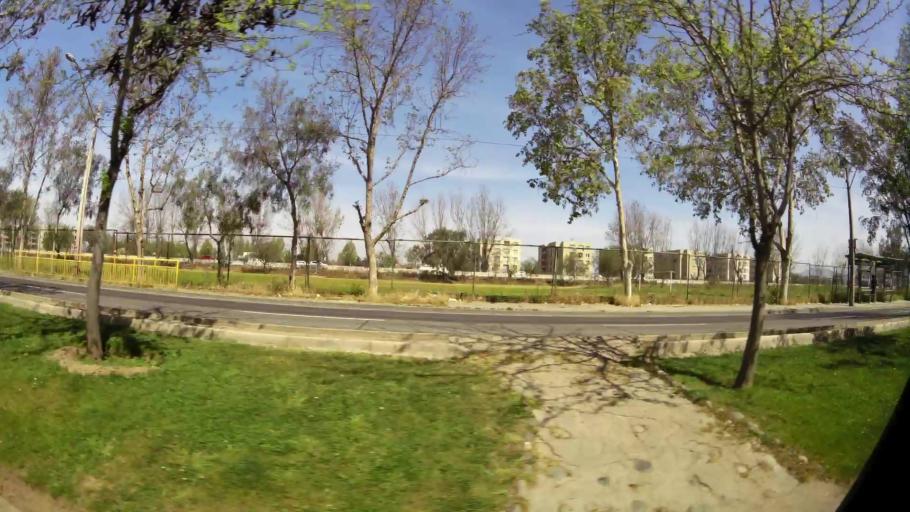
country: CL
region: Santiago Metropolitan
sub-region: Provincia de Santiago
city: Lo Prado
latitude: -33.4510
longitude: -70.7479
